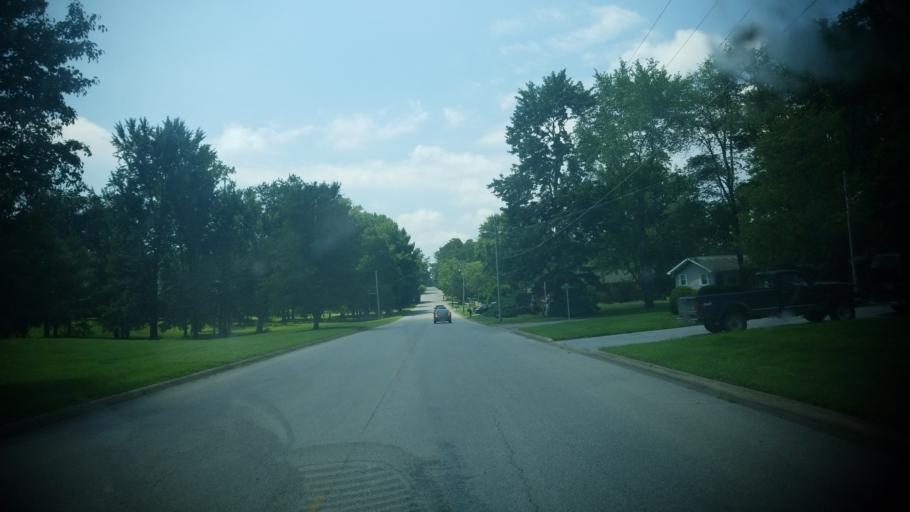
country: US
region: Illinois
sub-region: Wayne County
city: Fairfield
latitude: 38.3884
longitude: -88.3508
